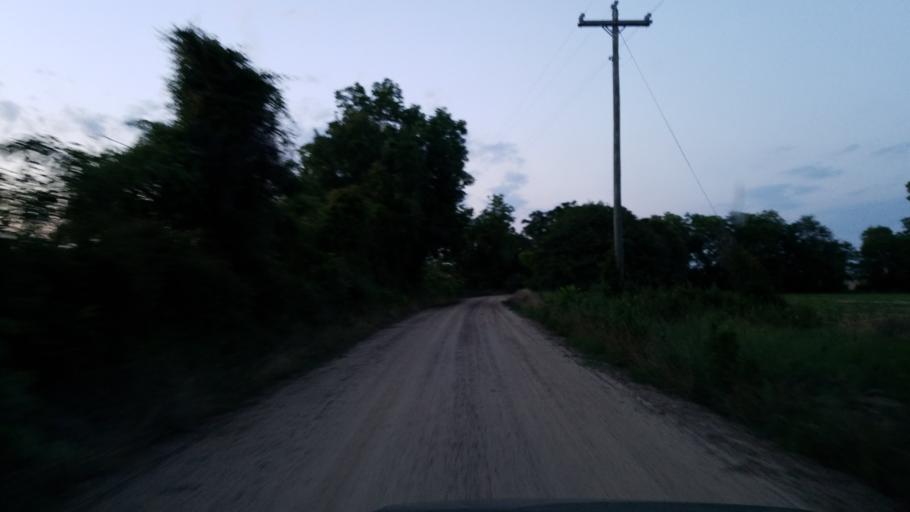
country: US
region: Georgia
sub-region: Turner County
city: Ashburn
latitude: 31.6583
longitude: -83.6272
